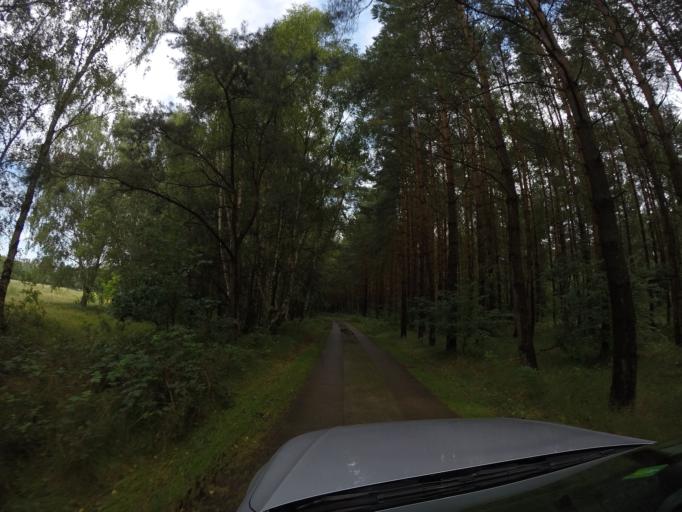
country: DE
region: Mecklenburg-Vorpommern
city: Wesenberg
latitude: 53.3775
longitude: 12.8947
